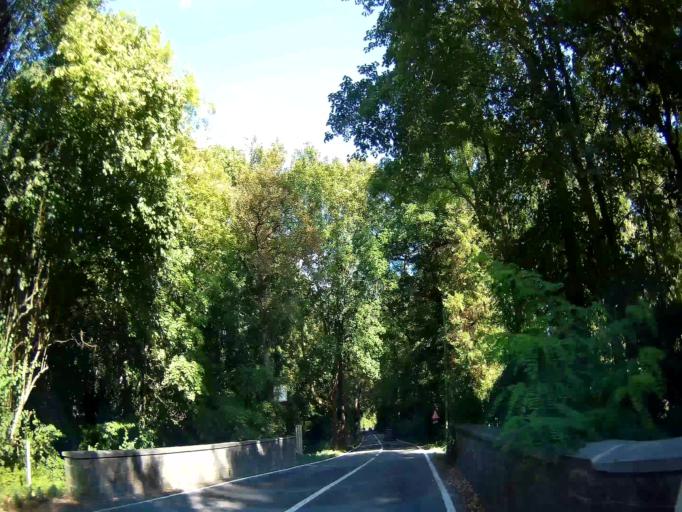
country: BE
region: Wallonia
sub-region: Province de Namur
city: Anhee
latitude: 50.3184
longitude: 4.8565
